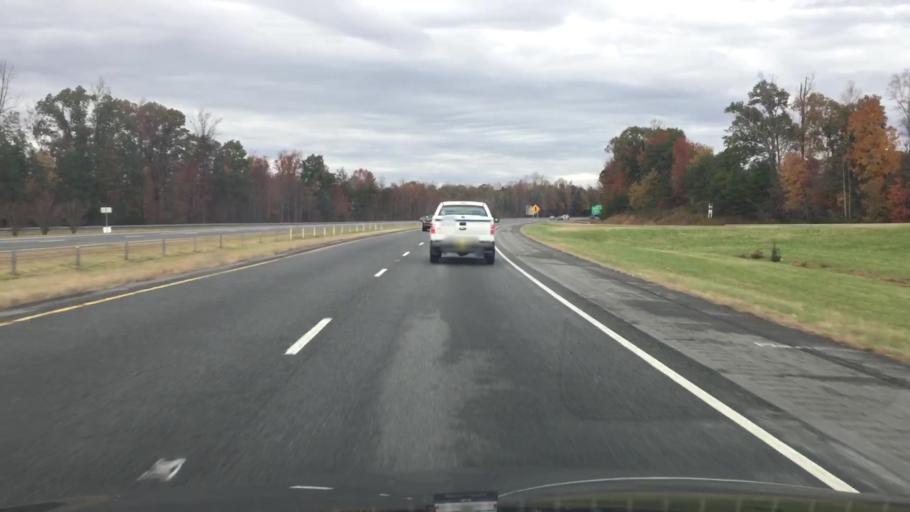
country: US
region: North Carolina
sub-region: Rockingham County
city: Reidsville
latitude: 36.3133
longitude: -79.6458
